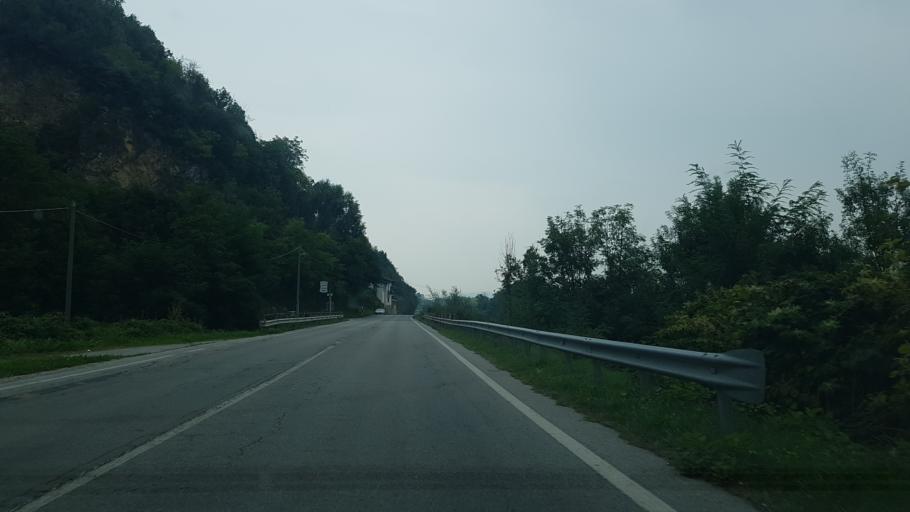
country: IT
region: Piedmont
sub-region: Provincia di Cuneo
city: Roccaforte Mondovi
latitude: 44.3309
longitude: 7.7536
